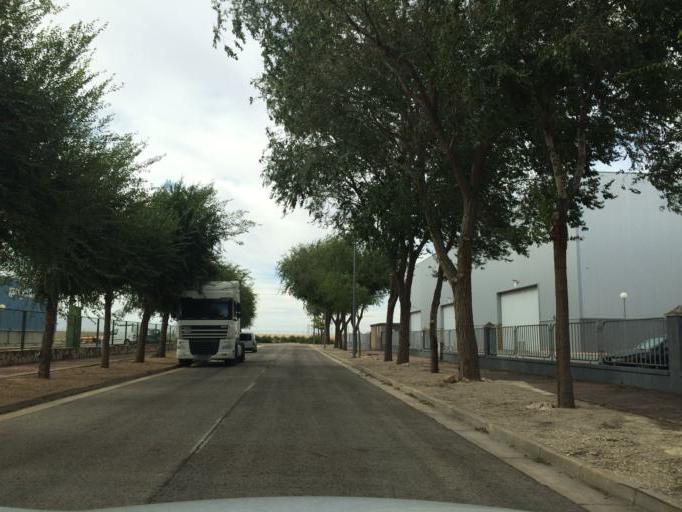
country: ES
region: Castille-La Mancha
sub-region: Provincia de Albacete
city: Albacete
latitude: 39.0214
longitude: -1.8899
